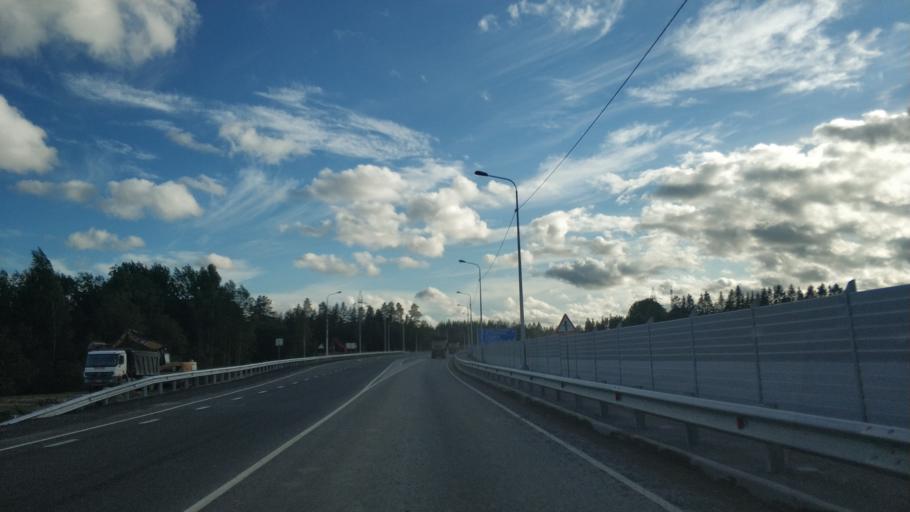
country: RU
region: Leningrad
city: Priozersk
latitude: 60.8499
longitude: 30.1474
